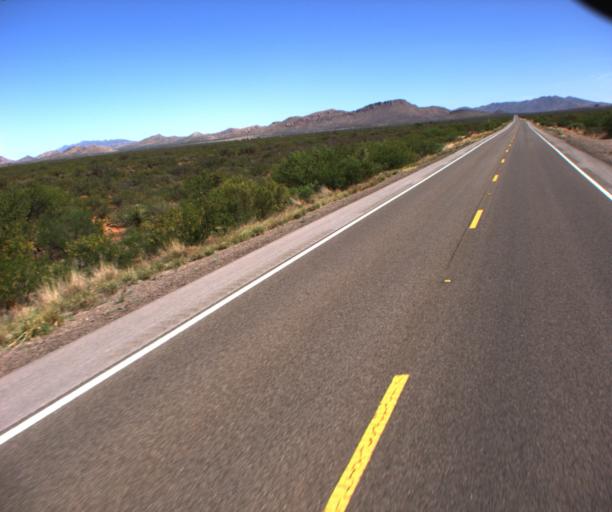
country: US
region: Arizona
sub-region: Cochise County
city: Douglas
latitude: 31.4174
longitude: -109.4927
